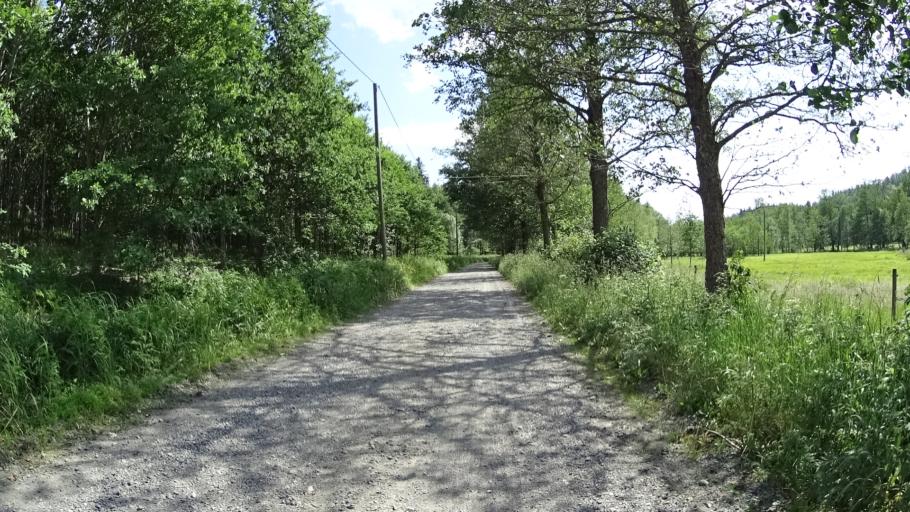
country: FI
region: Uusimaa
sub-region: Raaseporin
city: Pohja
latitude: 60.1231
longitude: 23.5381
